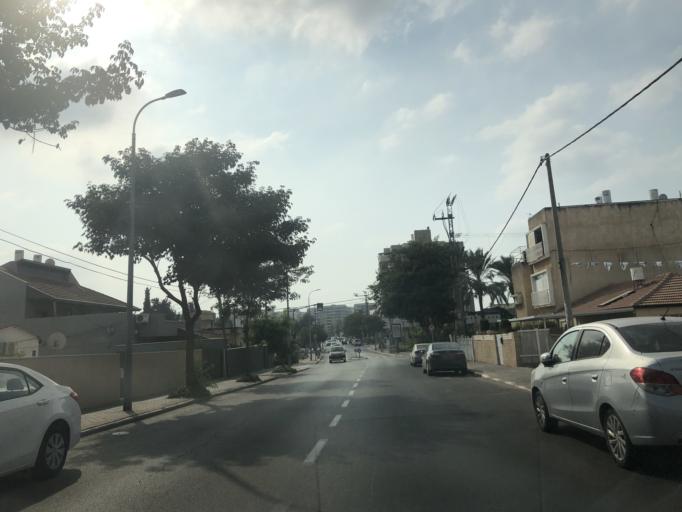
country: IL
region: Central District
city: Rosh Ha'Ayin
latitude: 32.0996
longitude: 34.9469
